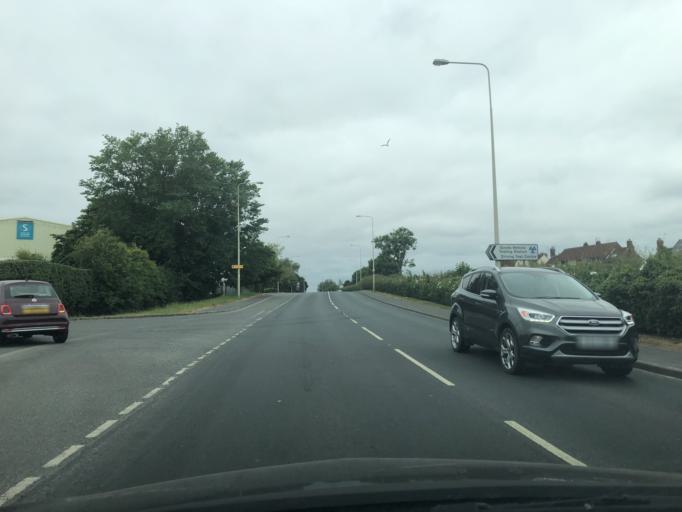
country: GB
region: England
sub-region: North Yorkshire
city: Scarborough
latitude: 54.2386
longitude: -0.4053
